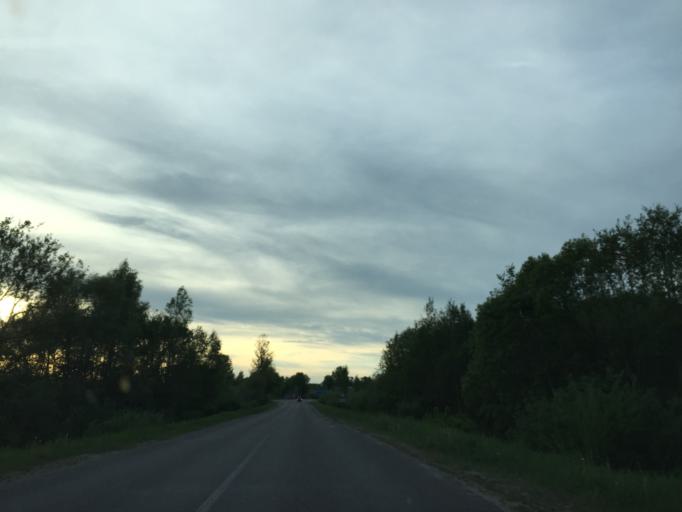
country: LV
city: Tireli
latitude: 56.8301
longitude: 23.5580
